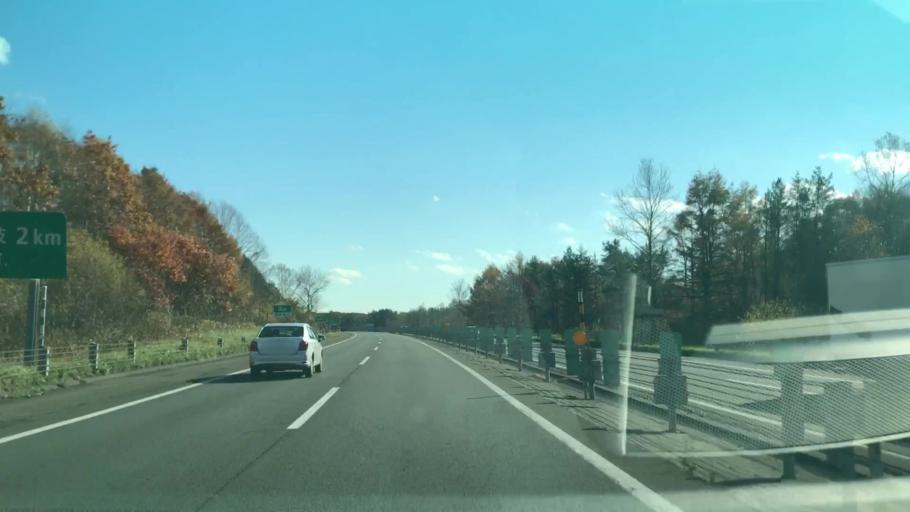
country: JP
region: Hokkaido
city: Chitose
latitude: 42.8568
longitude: 141.5625
